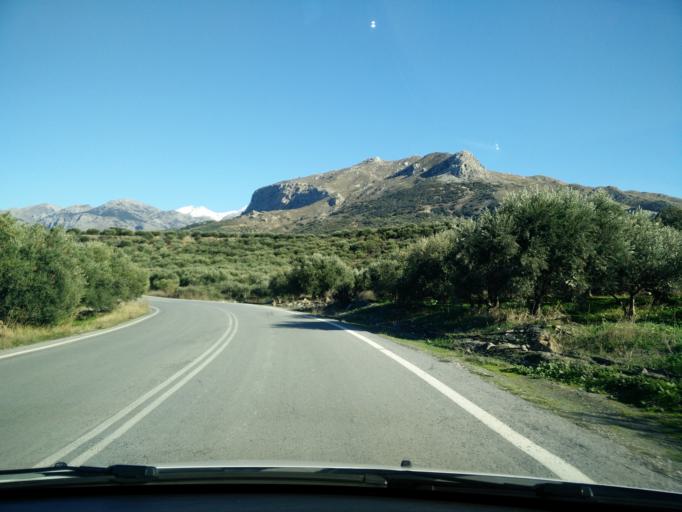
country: GR
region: Crete
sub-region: Nomos Irakleiou
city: Arkalochori
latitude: 35.0751
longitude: 25.3460
